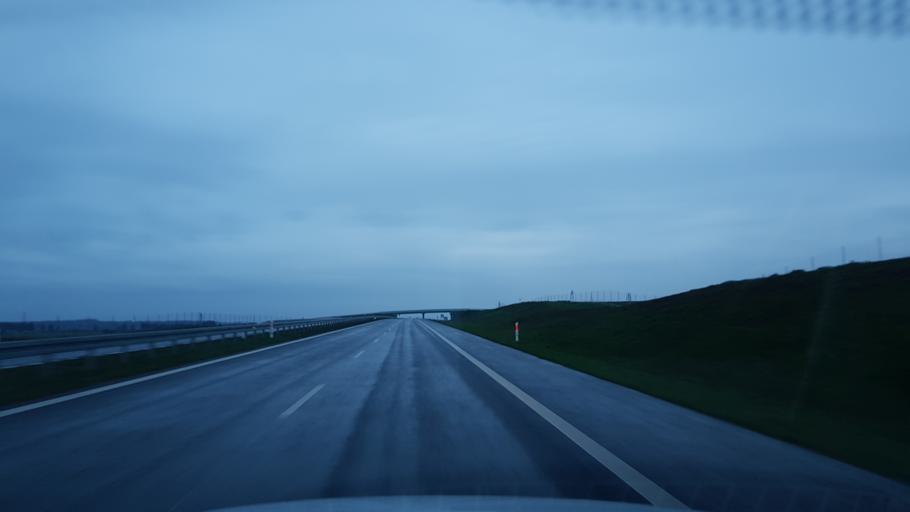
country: PL
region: West Pomeranian Voivodeship
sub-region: Powiat gryficki
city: Brojce
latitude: 53.9743
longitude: 15.4269
